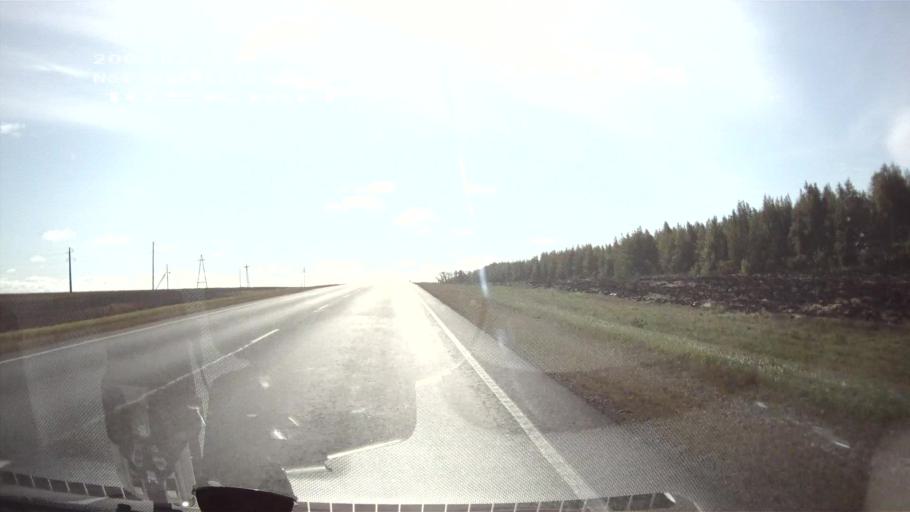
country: RU
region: Ulyanovsk
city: Tsil'na
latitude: 54.5839
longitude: 47.8868
